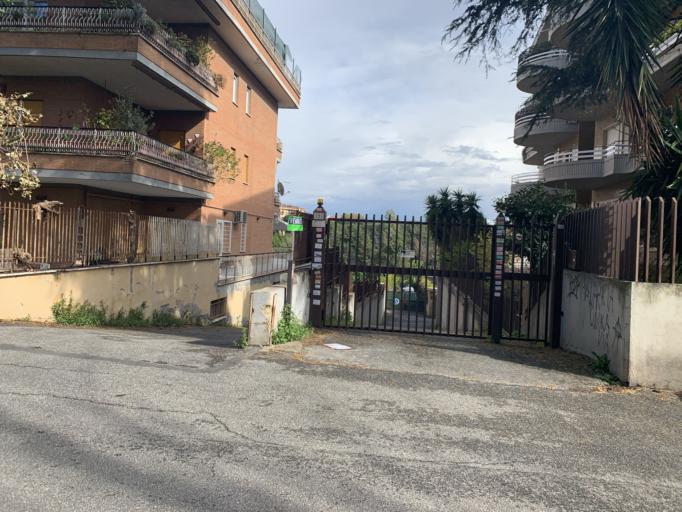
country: VA
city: Vatican City
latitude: 41.8789
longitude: 12.4184
